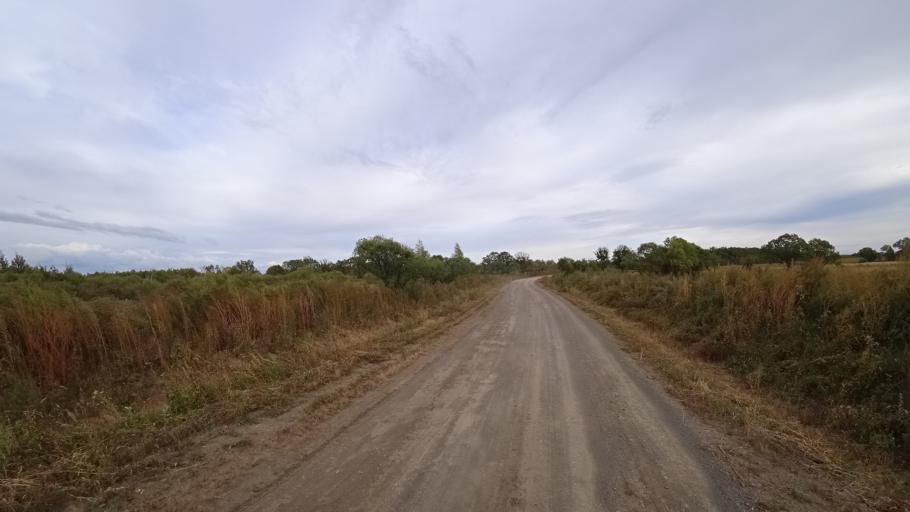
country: RU
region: Amur
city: Arkhara
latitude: 49.3528
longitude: 130.1467
